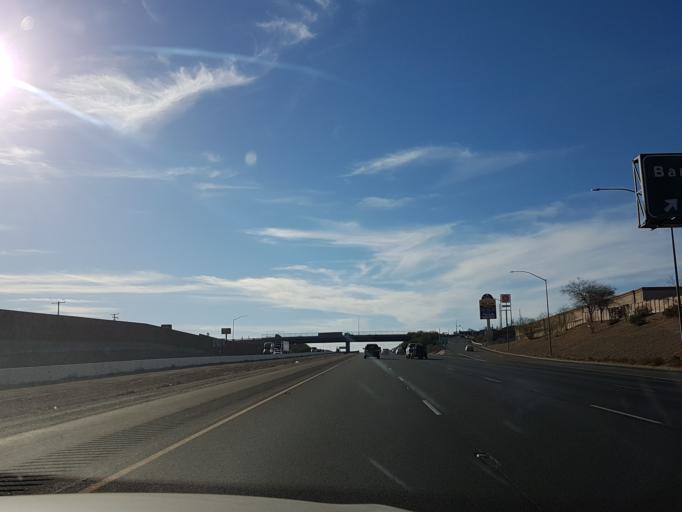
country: US
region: California
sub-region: San Bernardino County
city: Barstow
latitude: 34.8861
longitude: -117.0186
